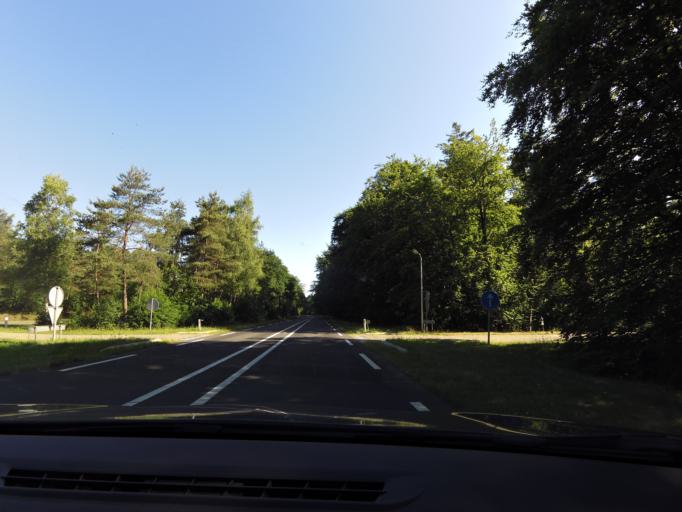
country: NL
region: Overijssel
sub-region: Gemeente Twenterand
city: Den Ham
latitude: 52.4758
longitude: 6.4273
